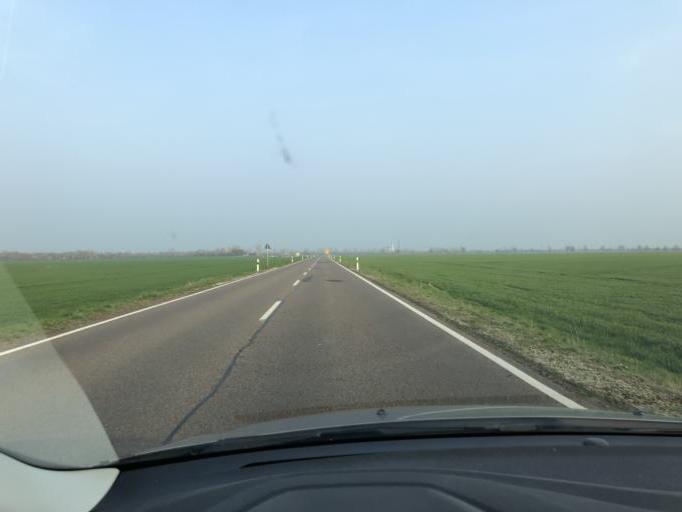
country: DE
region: Saxony-Anhalt
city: Roitzsch
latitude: 51.5317
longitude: 12.2909
